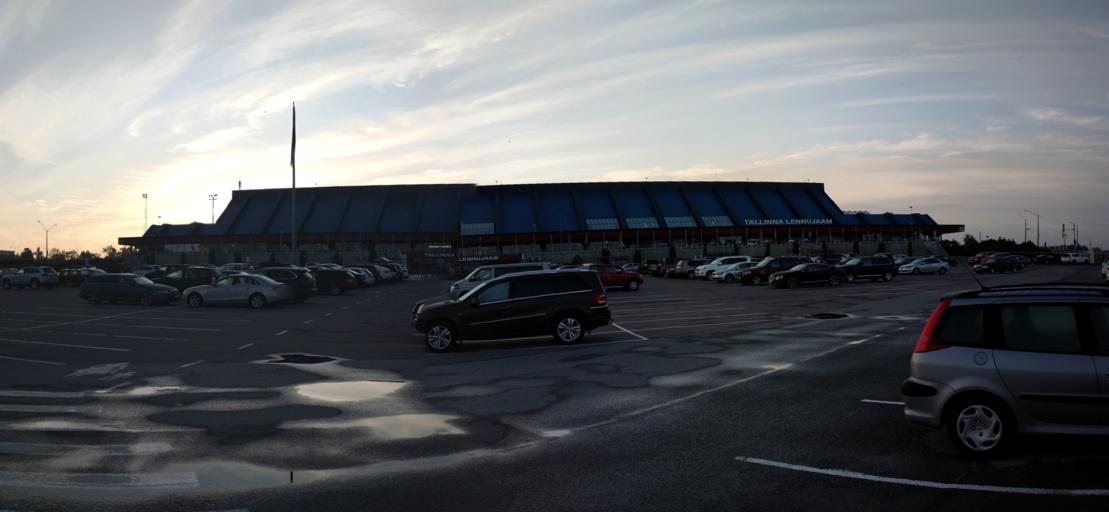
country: EE
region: Harju
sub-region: Tallinna linn
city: Tallinn
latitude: 59.4168
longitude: 24.7963
